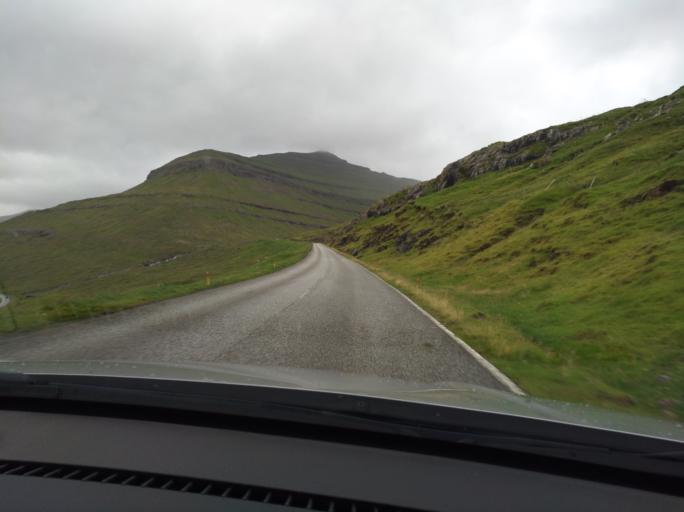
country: FO
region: Eysturoy
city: Fuglafjordur
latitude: 62.2184
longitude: -6.8668
